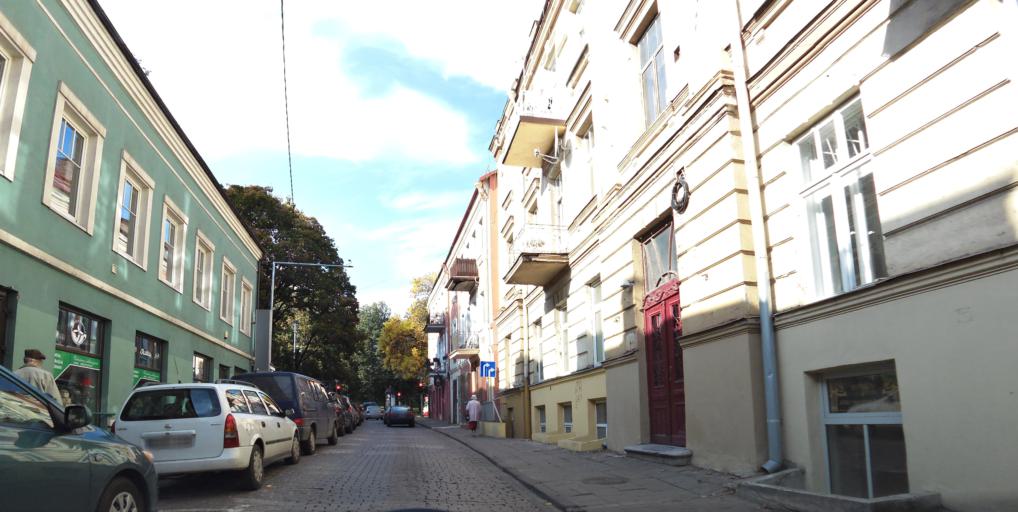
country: LT
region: Vilnius County
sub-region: Vilnius
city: Vilnius
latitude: 54.6819
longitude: 25.2784
